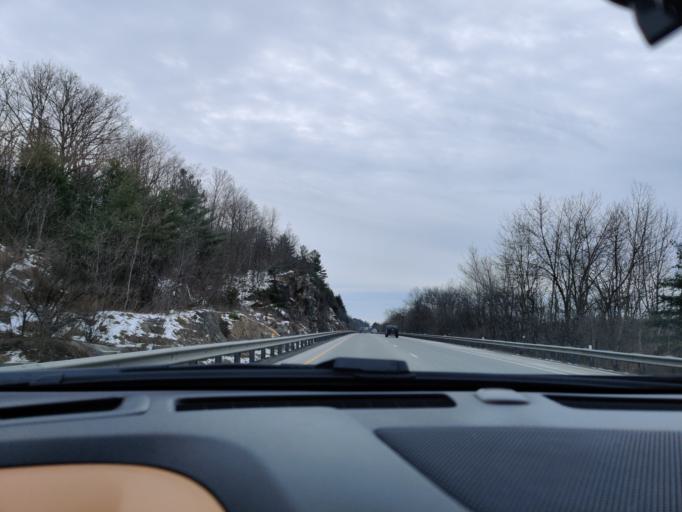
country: US
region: New York
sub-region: Jefferson County
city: Alexandria Bay
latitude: 44.4092
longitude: -75.9295
